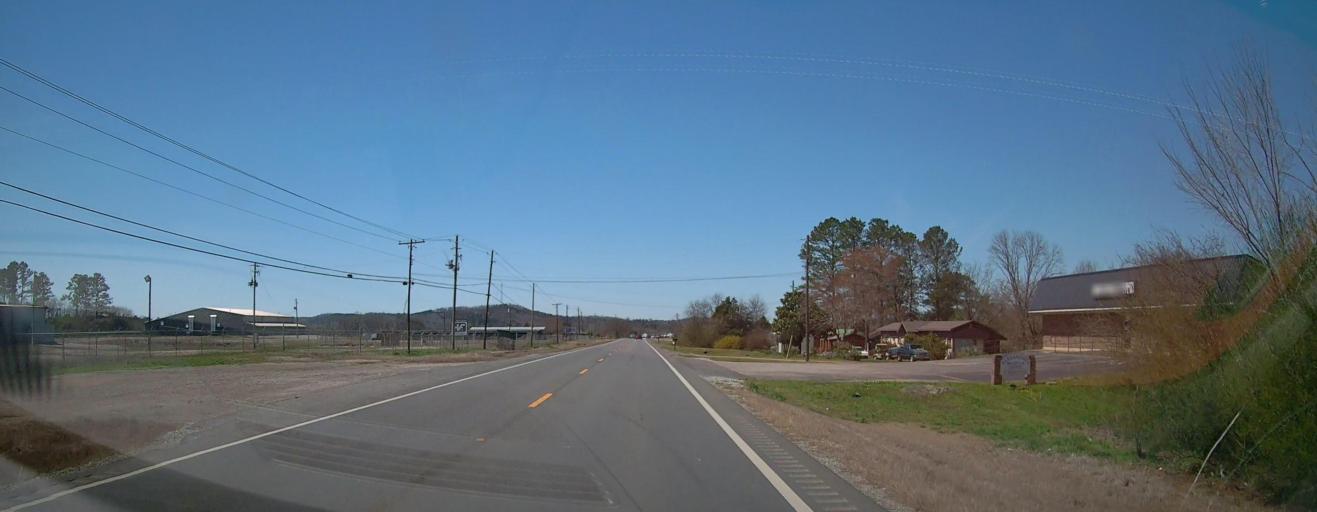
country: US
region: Alabama
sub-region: Calhoun County
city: Alexandria
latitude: 33.7826
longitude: -85.9109
